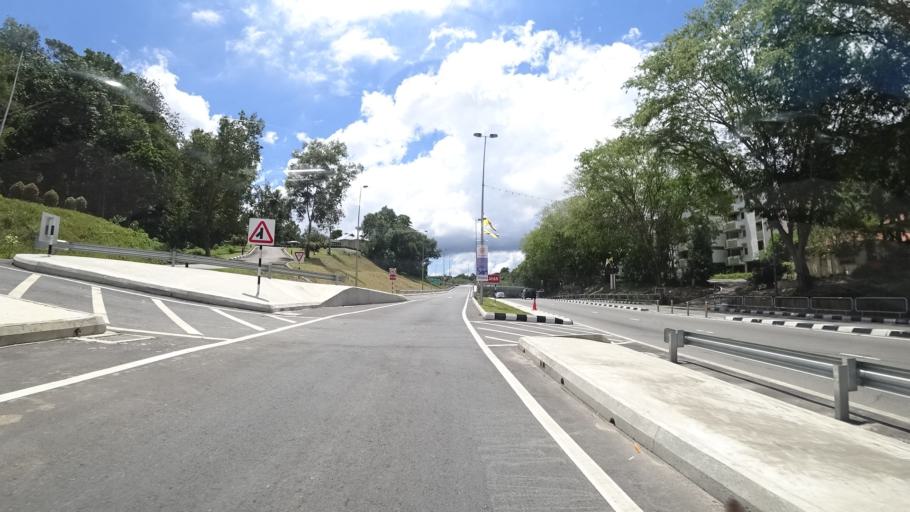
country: BN
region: Brunei and Muara
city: Bandar Seri Begawan
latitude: 4.8820
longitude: 114.9234
